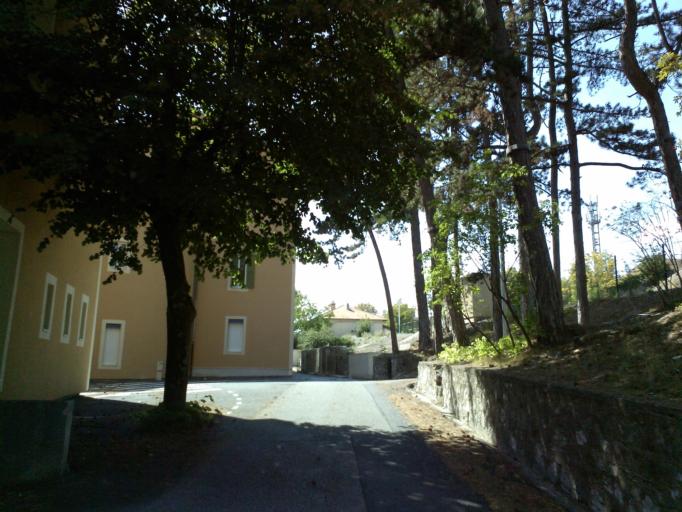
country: FR
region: Provence-Alpes-Cote d'Azur
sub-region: Departement des Alpes-de-Haute-Provence
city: Digne-les-Bains
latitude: 44.0910
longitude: 6.2275
